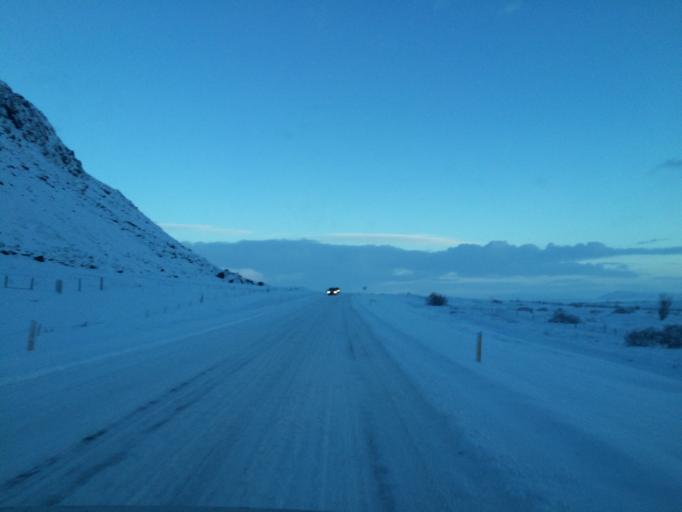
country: IS
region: South
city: Selfoss
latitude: 63.9595
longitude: -21.0087
